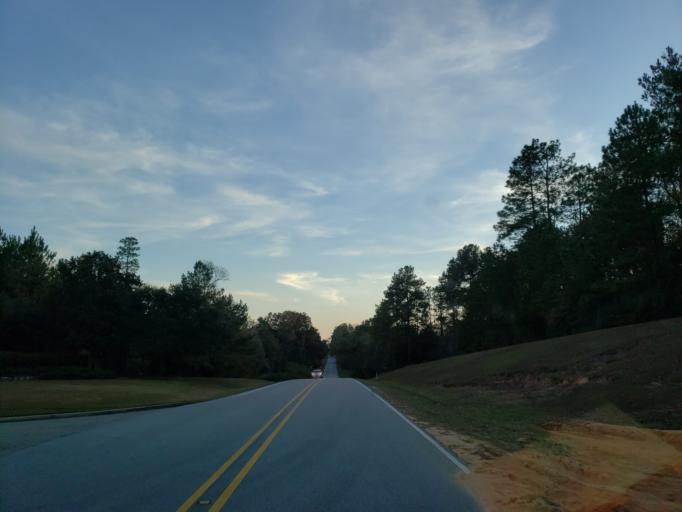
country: US
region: Mississippi
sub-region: Forrest County
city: Hattiesburg
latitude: 31.2579
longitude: -89.3141
